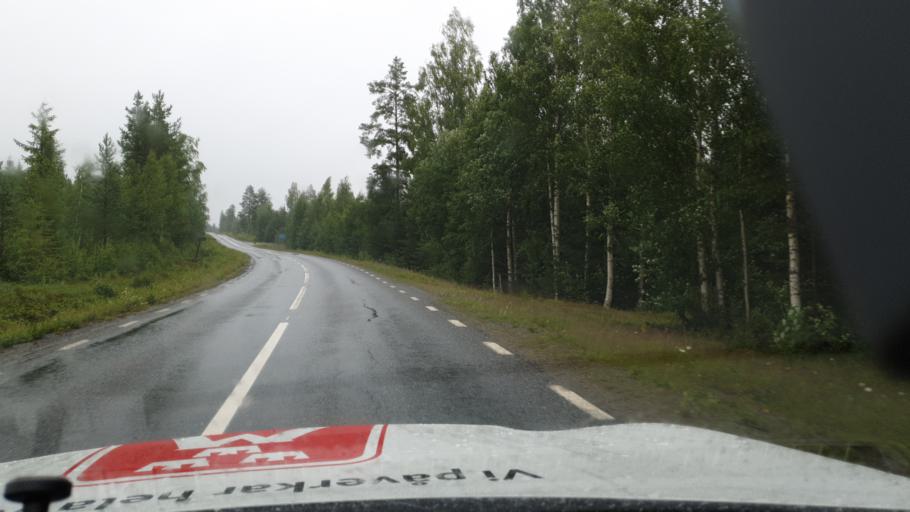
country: SE
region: Vaesterbotten
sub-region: Skelleftea Kommun
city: Burtraesk
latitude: 64.4788
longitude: 20.4226
